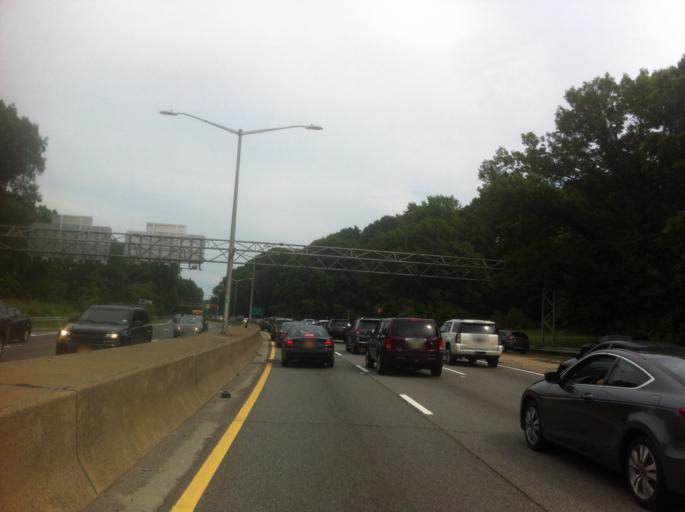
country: US
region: New York
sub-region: Nassau County
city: East Atlantic Beach
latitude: 40.7610
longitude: -73.7552
